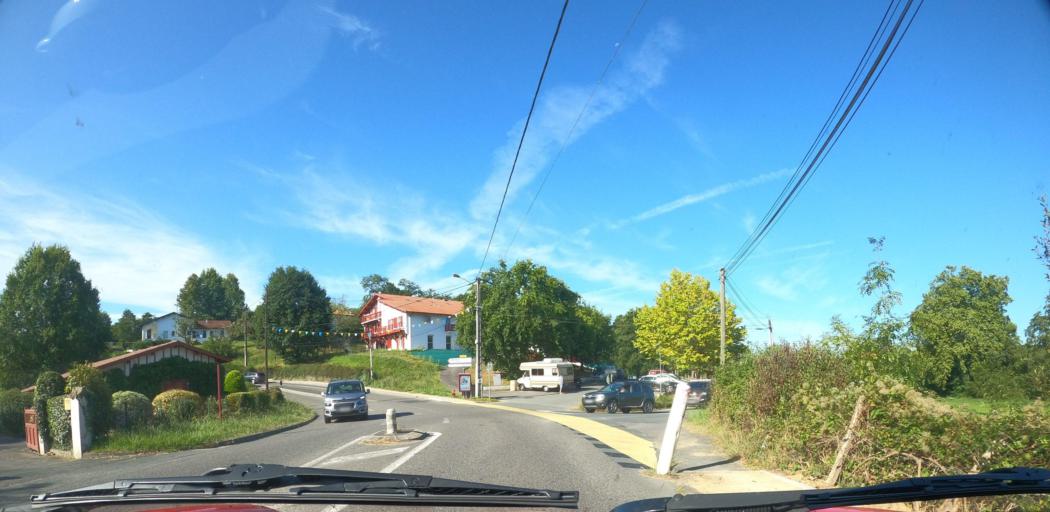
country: FR
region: Aquitaine
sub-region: Departement des Pyrenees-Atlantiques
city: Arbonne
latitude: 43.4361
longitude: -1.5526
